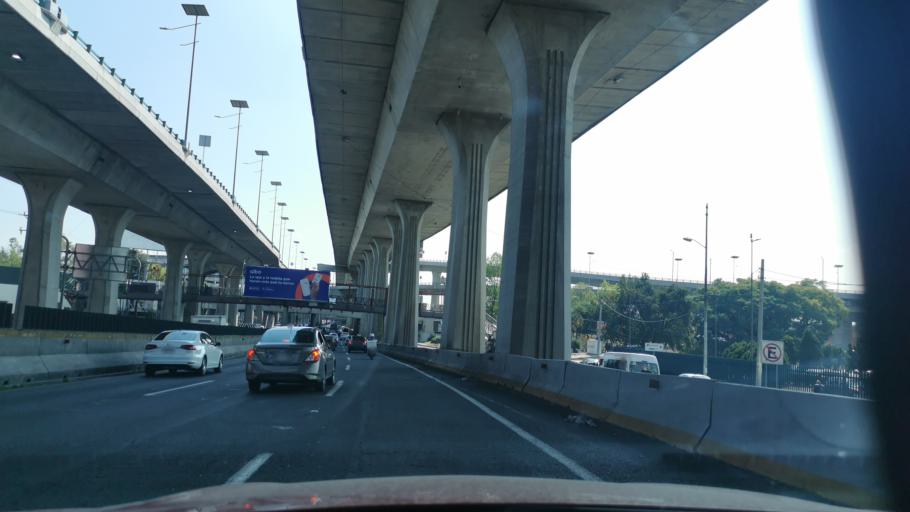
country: MX
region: Mexico
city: Naucalpan de Juarez
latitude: 19.4884
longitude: -99.2366
